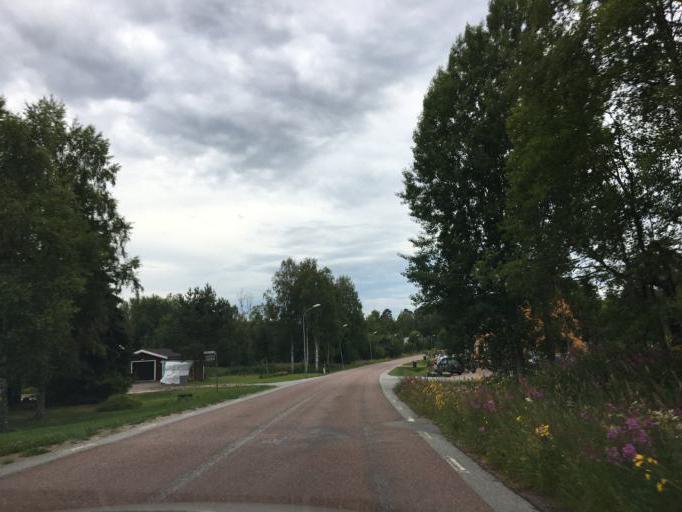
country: SE
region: Vaermland
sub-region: Filipstads Kommun
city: Lesjofors
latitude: 60.1422
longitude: 14.3899
